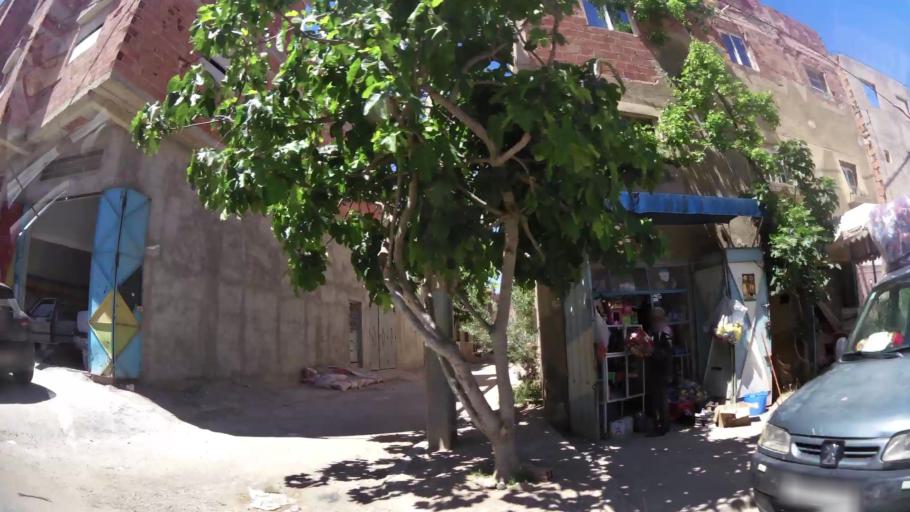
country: MA
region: Oriental
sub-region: Oujda-Angad
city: Oujda
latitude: 34.6604
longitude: -1.8804
